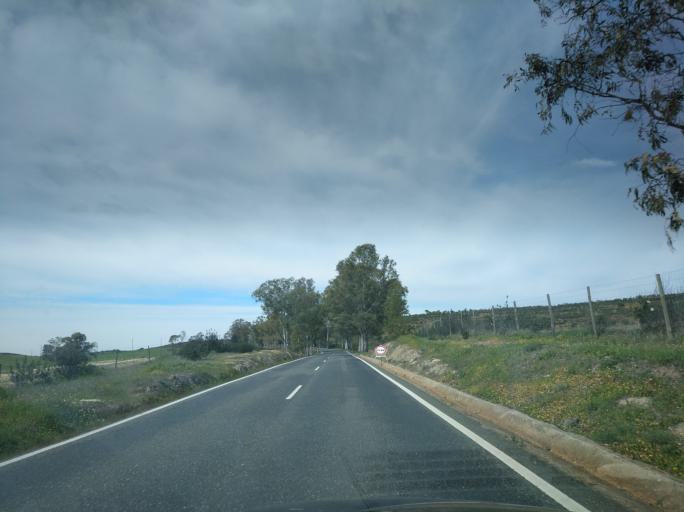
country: PT
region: Beja
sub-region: Mertola
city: Mertola
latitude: 37.7045
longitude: -7.7493
